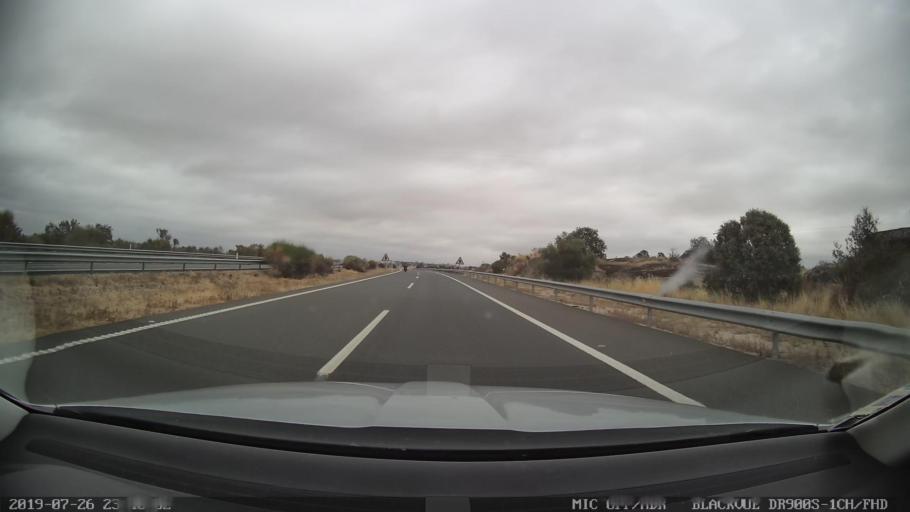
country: ES
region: Extremadura
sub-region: Provincia de Caceres
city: Trujillo
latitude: 39.4557
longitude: -5.8631
